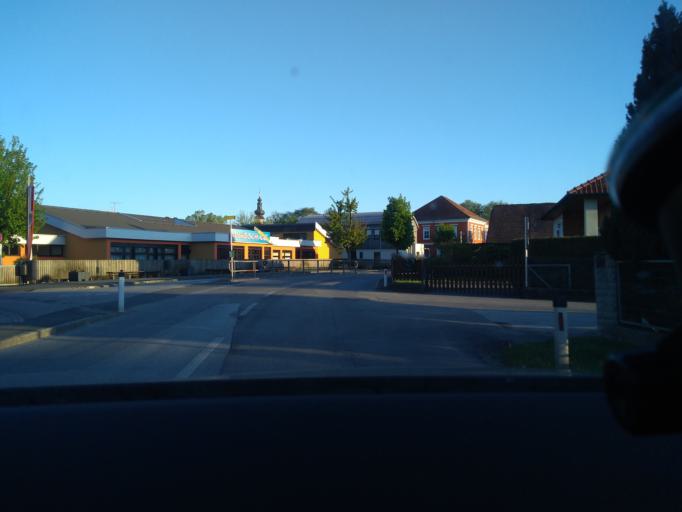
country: AT
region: Styria
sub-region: Politischer Bezirk Voitsberg
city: Mooskirchen
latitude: 46.9874
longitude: 15.2816
